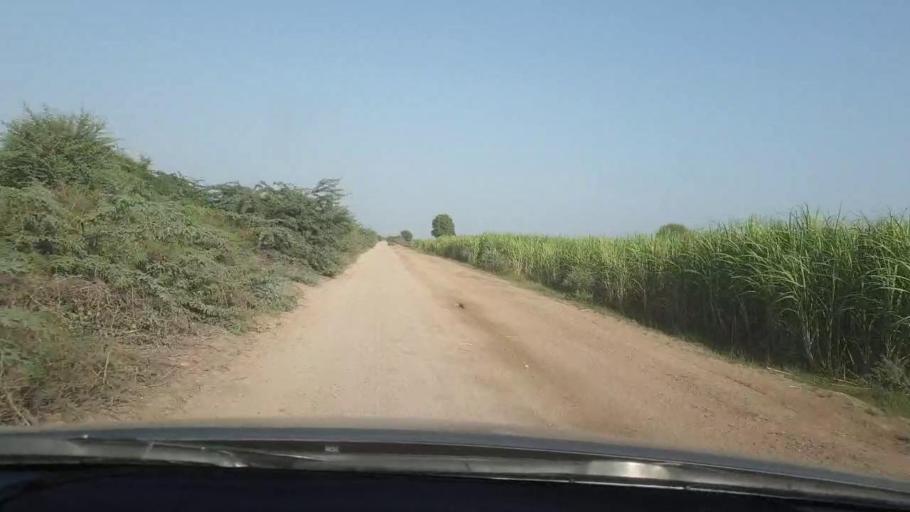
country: PK
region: Sindh
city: Naukot
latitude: 24.7781
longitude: 69.2716
